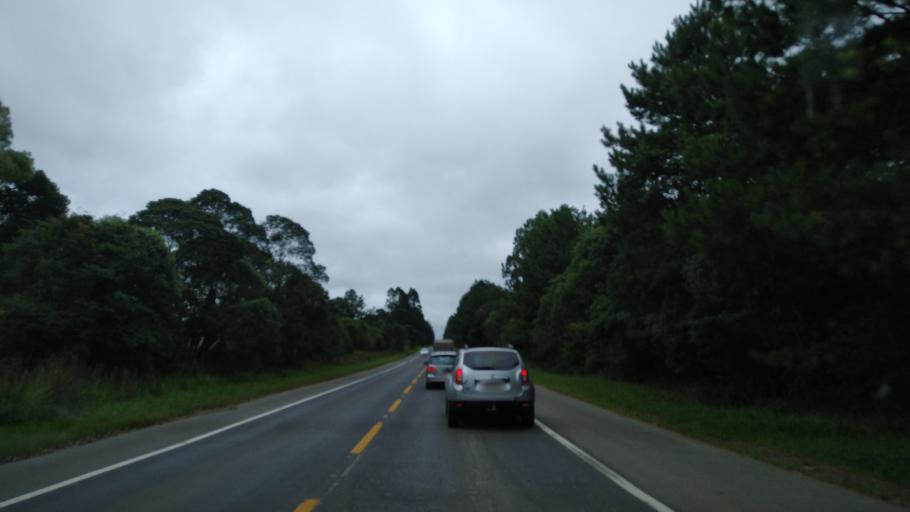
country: BR
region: Santa Catarina
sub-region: Tres Barras
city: Tres Barras
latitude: -26.1827
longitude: -50.2131
